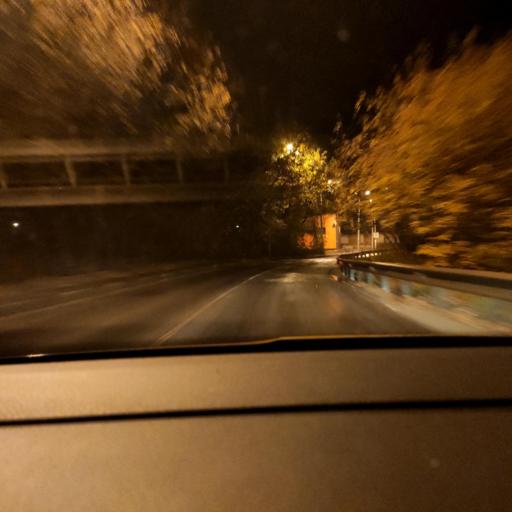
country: RU
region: Moskovskaya
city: Ivanteyevka
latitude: 55.9636
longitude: 37.9355
